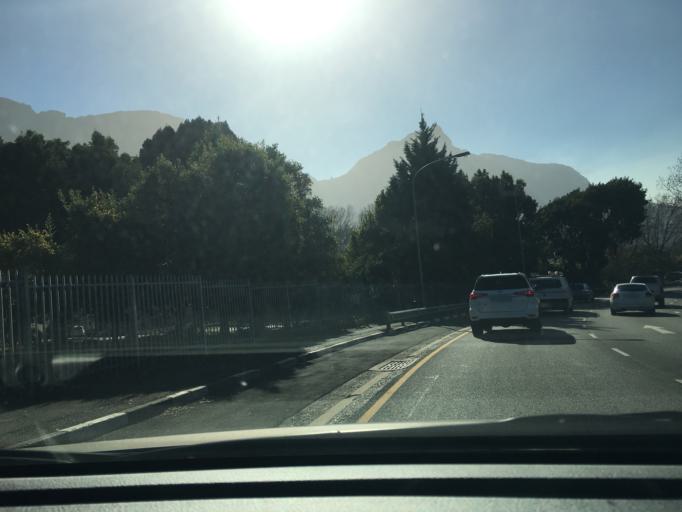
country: ZA
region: Western Cape
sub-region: City of Cape Town
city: Newlands
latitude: -33.9867
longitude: 18.4515
